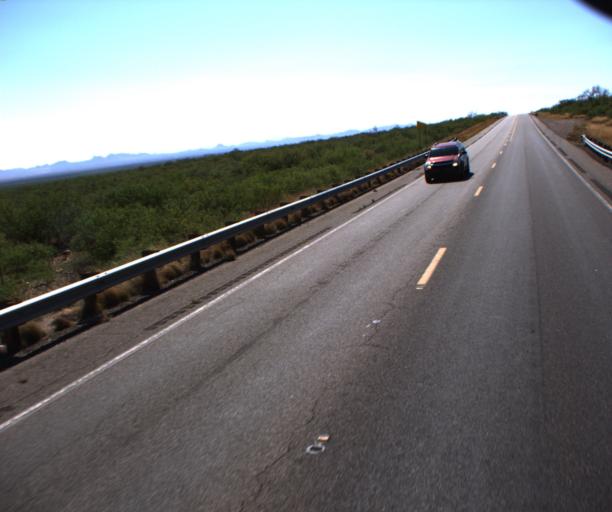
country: US
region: Arizona
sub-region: Cochise County
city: Bisbee
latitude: 31.4307
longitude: -109.8104
